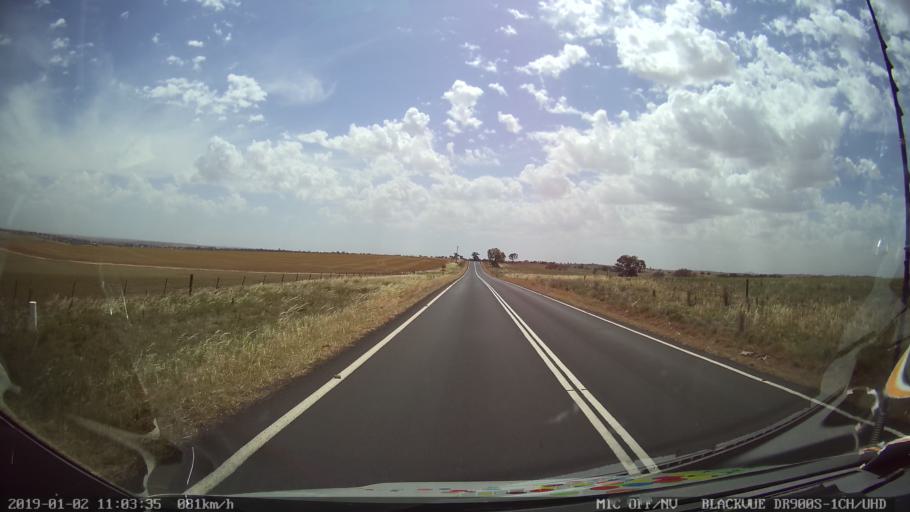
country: AU
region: New South Wales
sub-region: Young
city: Young
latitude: -34.5772
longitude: 148.3397
